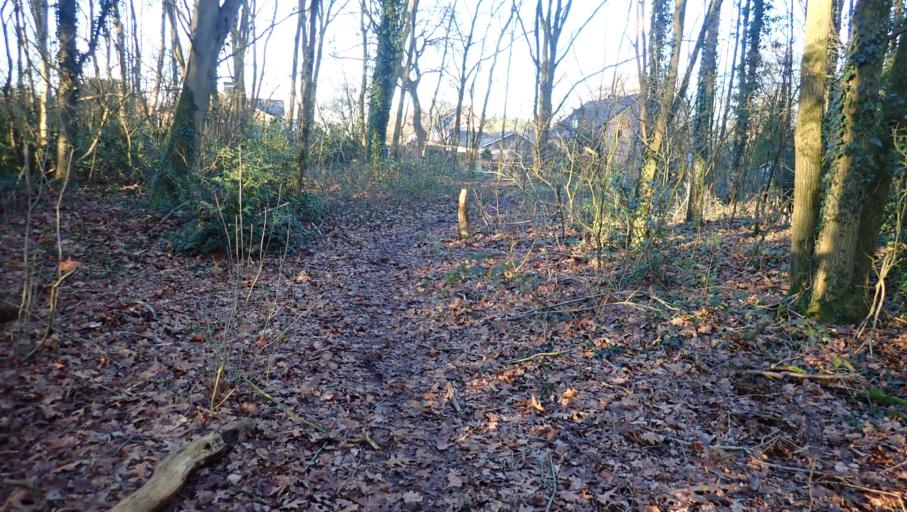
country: BE
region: Flanders
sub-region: Provincie Antwerpen
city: Zandhoven
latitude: 51.2394
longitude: 4.6558
